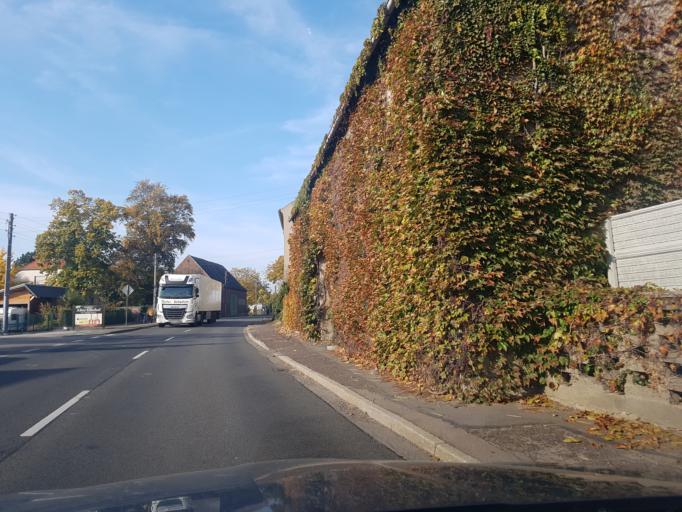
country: DE
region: Saxony
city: Beilrode
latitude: 51.5534
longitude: 13.0337
